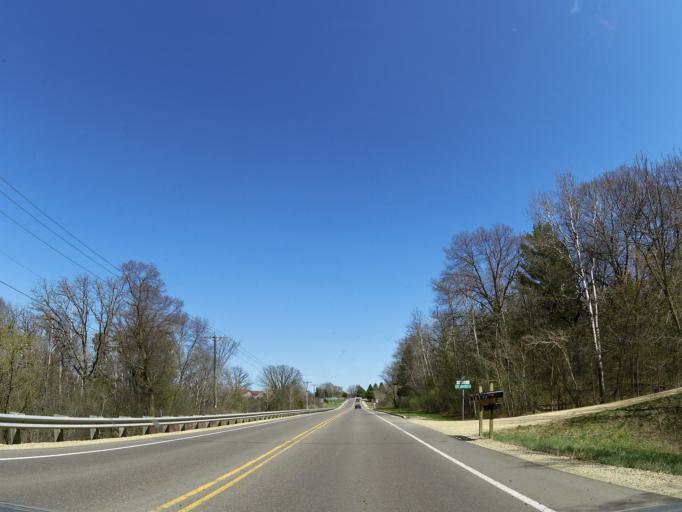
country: US
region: Wisconsin
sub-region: Saint Croix County
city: Hudson
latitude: 44.9595
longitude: -92.6860
